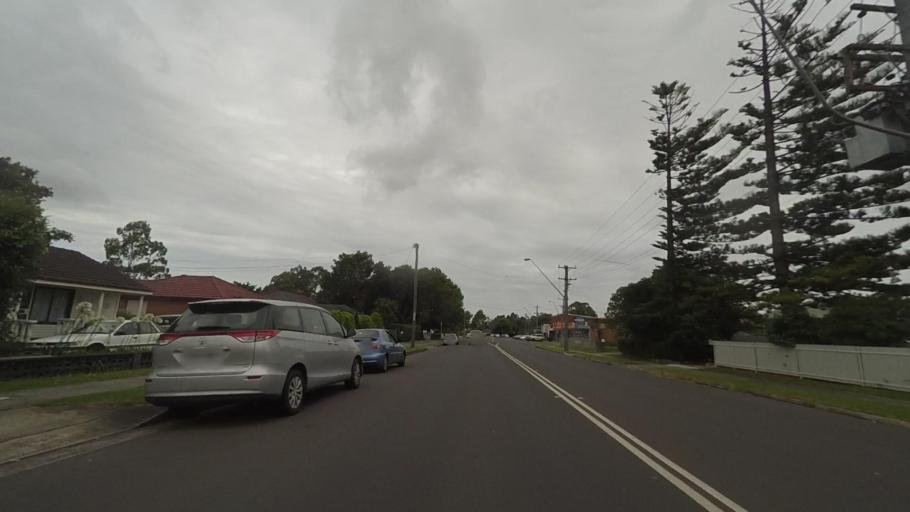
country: AU
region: New South Wales
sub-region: Wollongong
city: Cordeaux Heights
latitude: -34.4593
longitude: 150.8384
